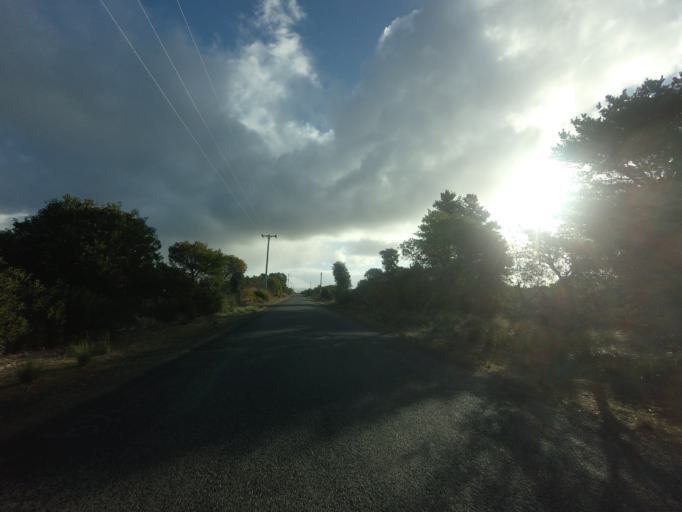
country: AU
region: Tasmania
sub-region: Break O'Day
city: St Helens
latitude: -42.0886
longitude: 148.1418
